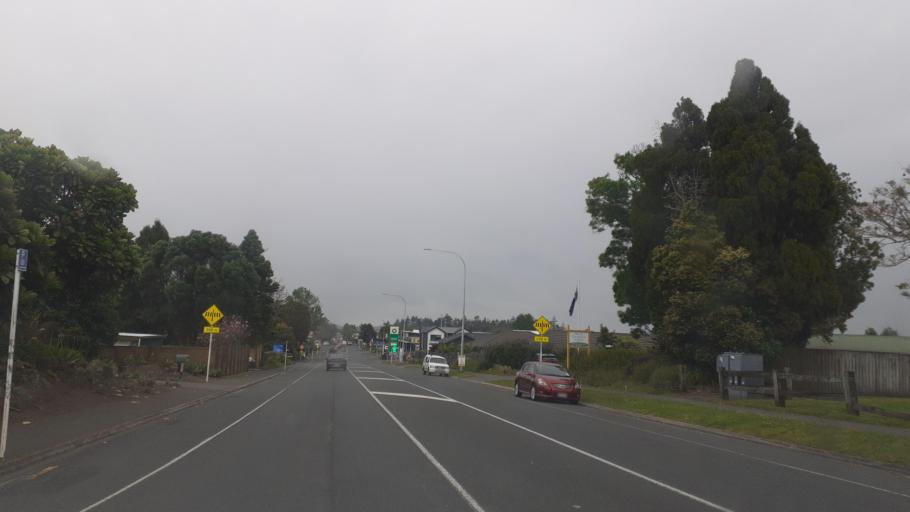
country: NZ
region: Northland
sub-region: Far North District
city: Kerikeri
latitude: -35.2321
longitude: 173.9448
